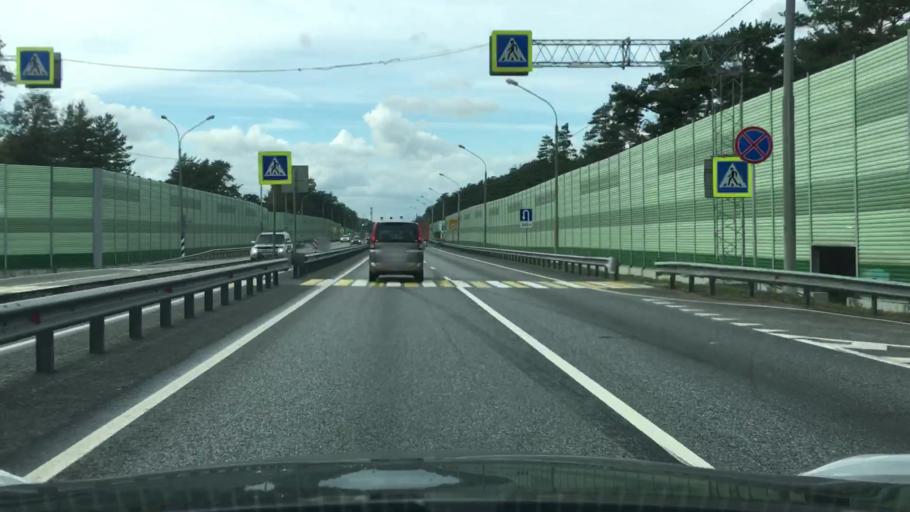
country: RU
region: Tverskaya
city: Radchenko
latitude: 56.6779
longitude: 36.3961
